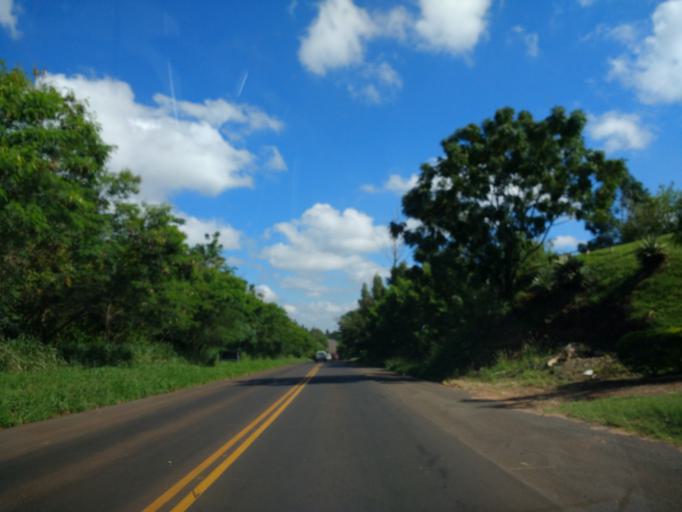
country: BR
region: Parana
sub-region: Umuarama
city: Umuarama
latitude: -23.8168
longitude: -53.3316
